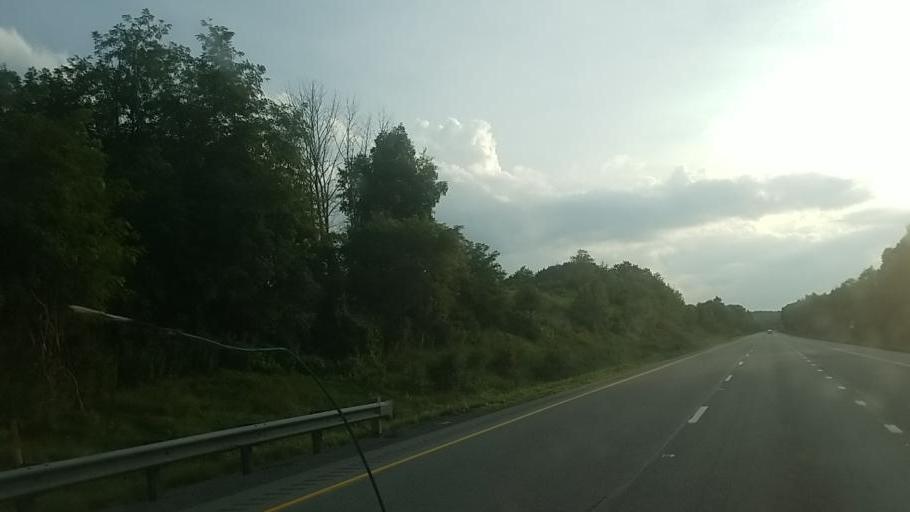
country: US
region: Pennsylvania
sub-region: Clearfield County
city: Troy
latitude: 40.9878
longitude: -78.1736
